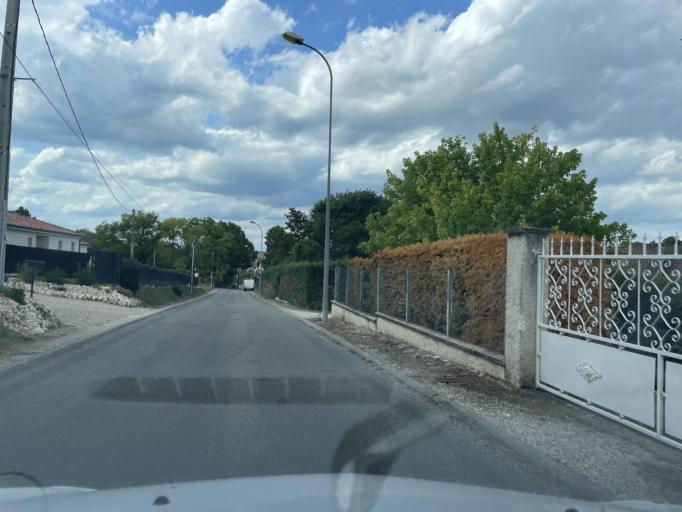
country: FR
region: Aquitaine
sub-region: Departement du Lot-et-Garonne
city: Casteljaloux
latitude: 44.3110
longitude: 0.0959
